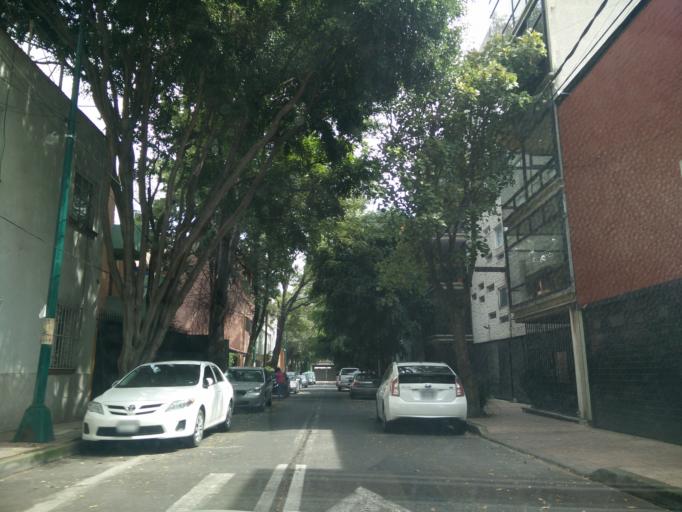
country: MX
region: Mexico City
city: Polanco
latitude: 19.4132
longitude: -99.1860
